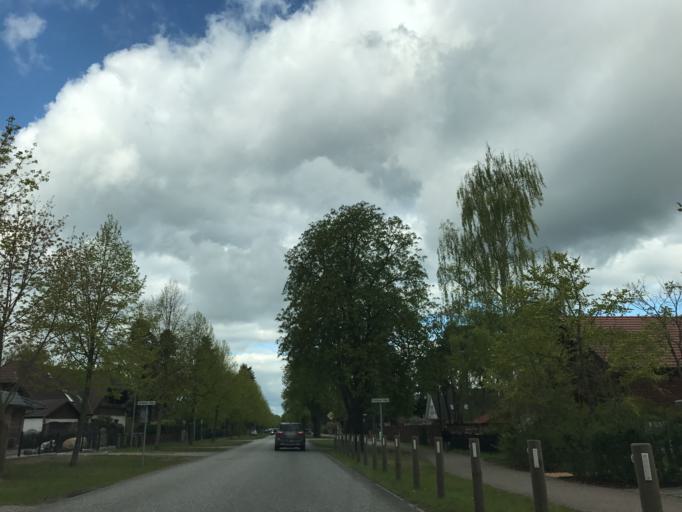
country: DE
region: Brandenburg
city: Brieselang
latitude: 52.5844
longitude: 12.9862
